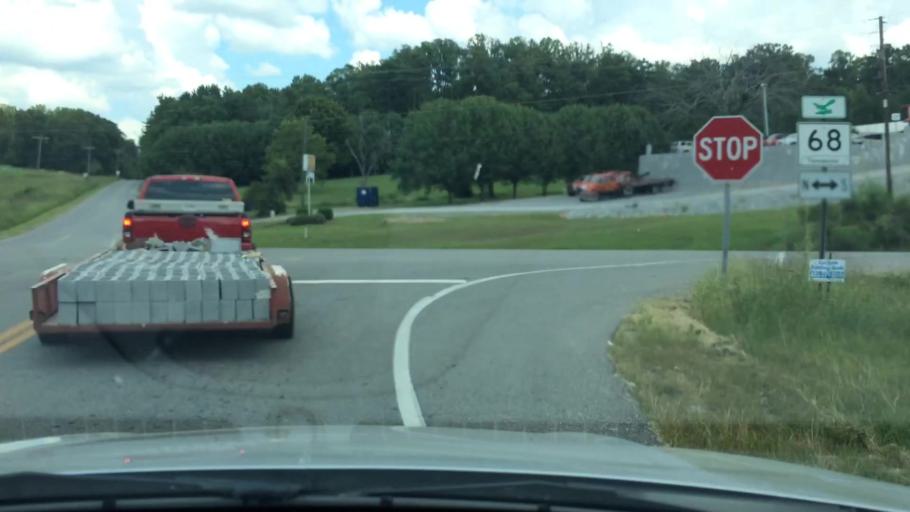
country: US
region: Tennessee
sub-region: Monroe County
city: Sweetwater
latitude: 35.5371
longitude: -84.4424
